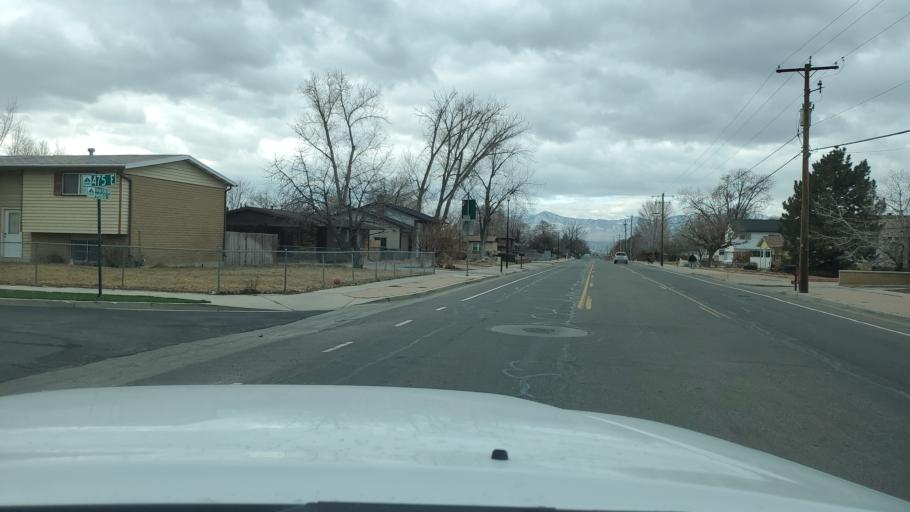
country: US
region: Utah
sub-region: Salt Lake County
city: White City
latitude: 40.5733
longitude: -111.8776
